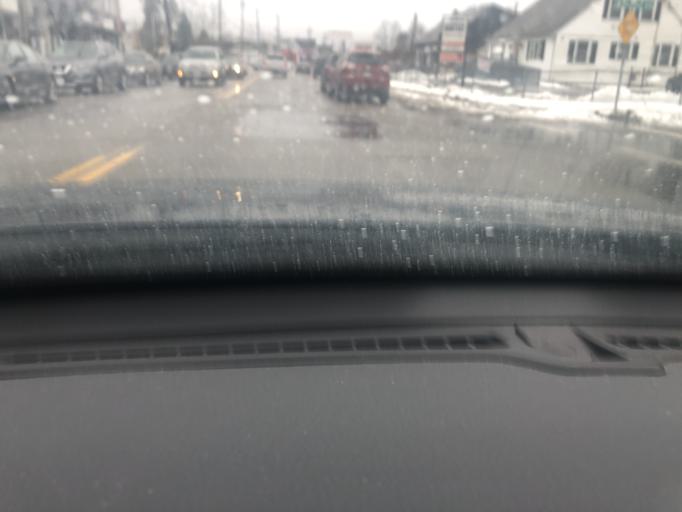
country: US
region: Massachusetts
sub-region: Plymouth County
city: Brockton
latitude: 42.1044
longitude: -71.0245
